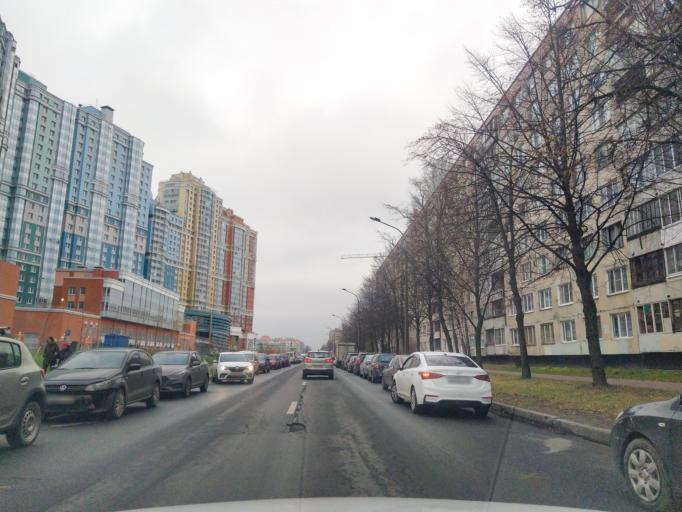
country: RU
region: St.-Petersburg
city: Sosnovka
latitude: 60.0428
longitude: 30.3636
